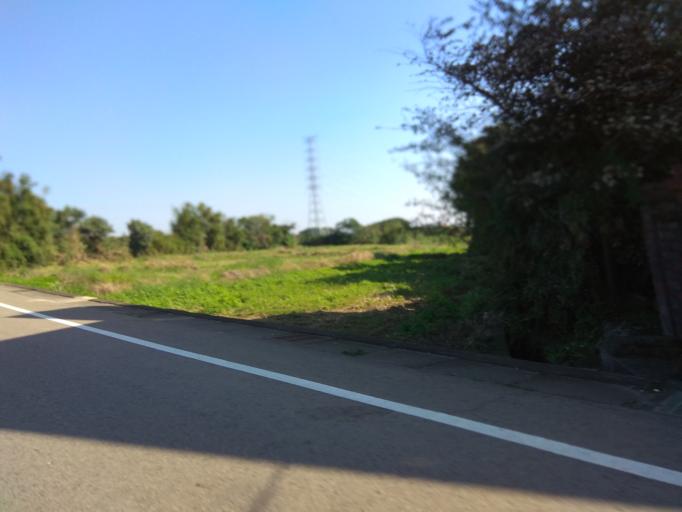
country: TW
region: Taiwan
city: Taoyuan City
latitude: 25.0357
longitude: 121.1128
